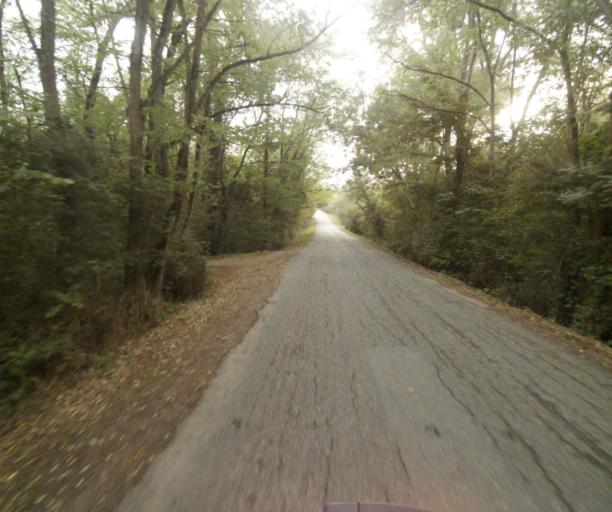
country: FR
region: Midi-Pyrenees
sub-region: Departement du Tarn-et-Garonne
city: Montech
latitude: 43.9344
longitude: 1.2551
